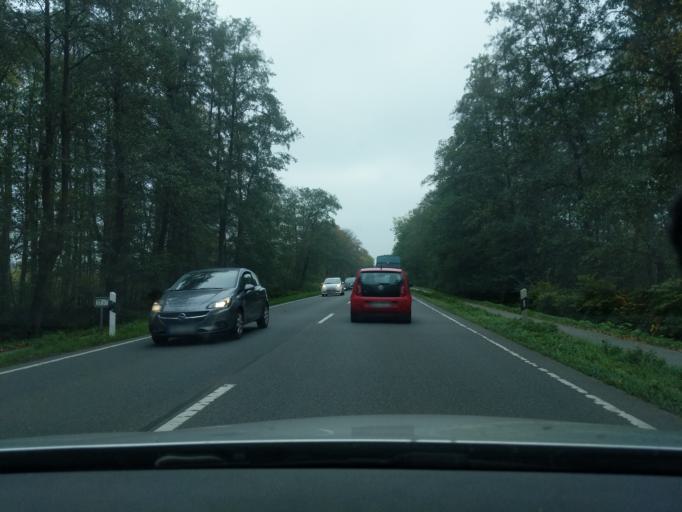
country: DE
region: Lower Saxony
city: Burweg
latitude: 53.6298
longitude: 9.2609
